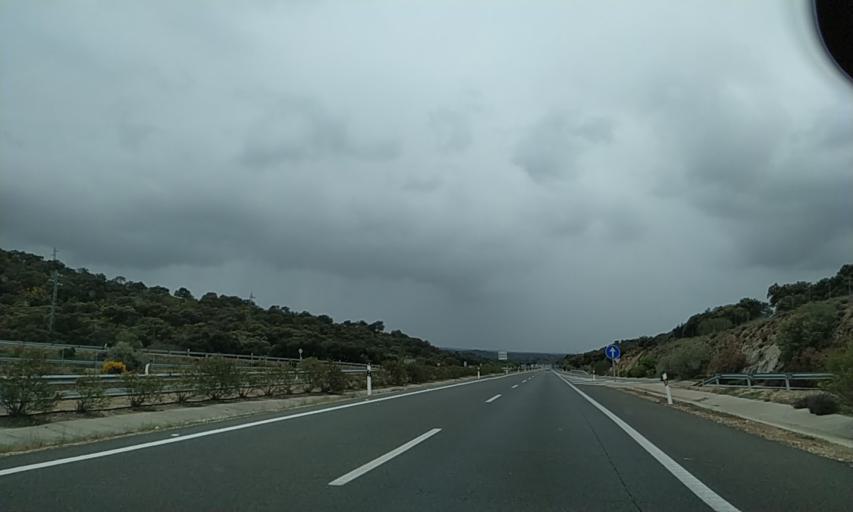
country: ES
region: Extremadura
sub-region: Provincia de Caceres
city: Oliva de Plasencia
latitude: 40.0822
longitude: -6.0829
